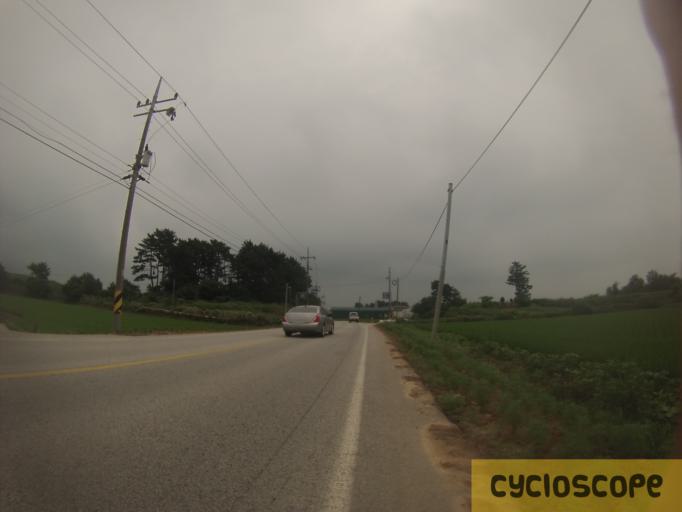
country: KR
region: Jeollabuk-do
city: Iksan
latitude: 35.9182
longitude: 126.8346
